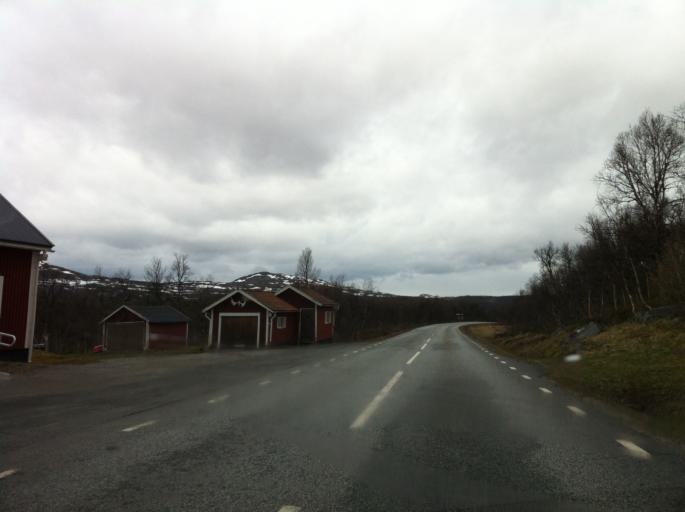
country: NO
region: Sor-Trondelag
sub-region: Tydal
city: Aas
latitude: 62.6077
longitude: 12.1615
